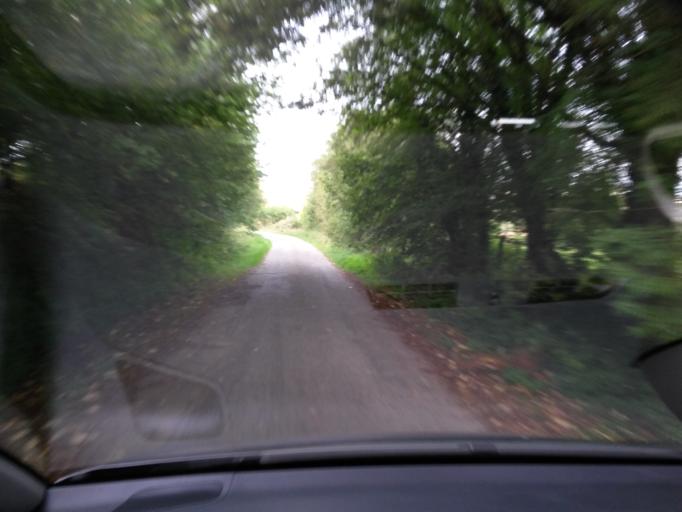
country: BE
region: Wallonia
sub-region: Province du Luxembourg
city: Etalle
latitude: 49.6769
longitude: 5.6264
